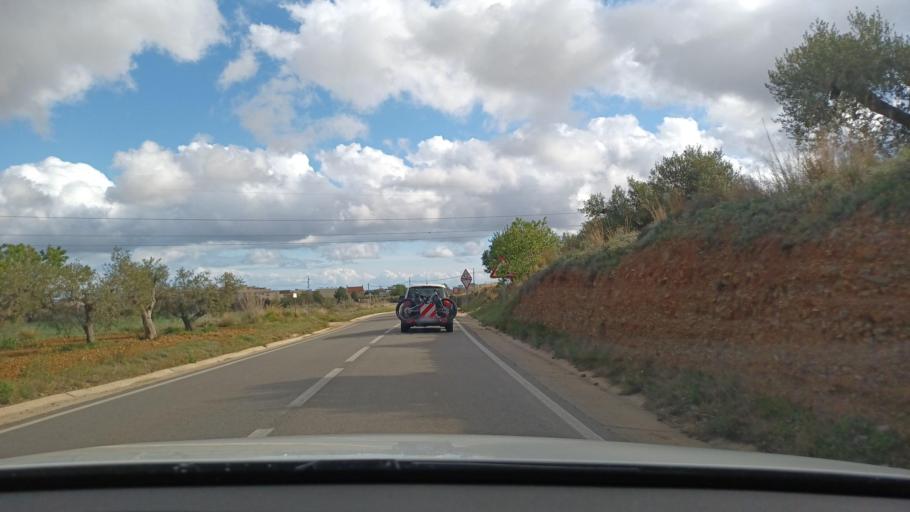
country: ES
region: Catalonia
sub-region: Provincia de Tarragona
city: Botarell
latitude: 41.1268
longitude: 0.9968
